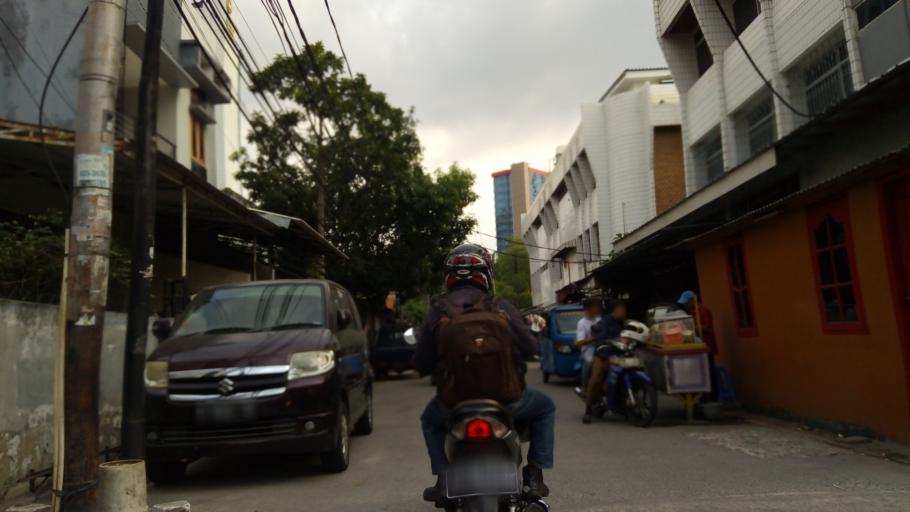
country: ID
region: Jakarta Raya
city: Jakarta
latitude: -6.1455
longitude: 106.8354
